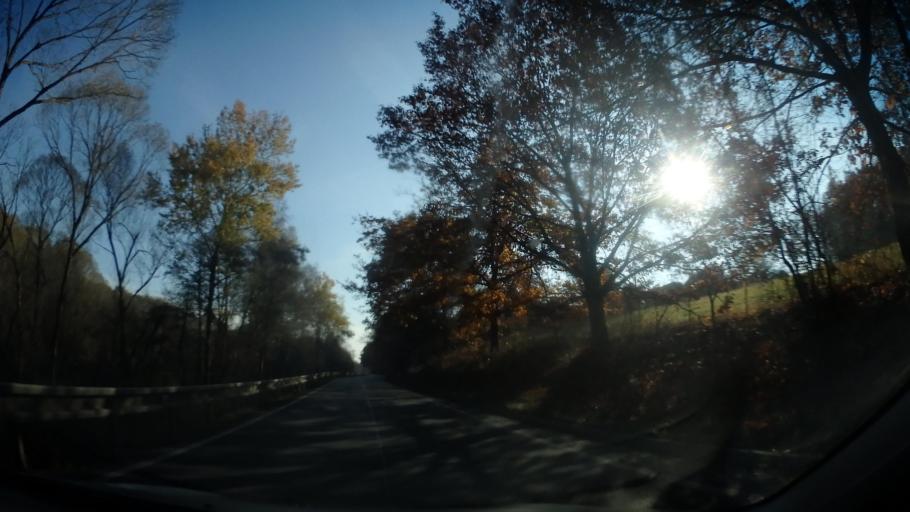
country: CZ
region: Central Bohemia
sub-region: Okres Praha-Vychod
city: Mnichovice
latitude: 49.9215
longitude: 14.7201
